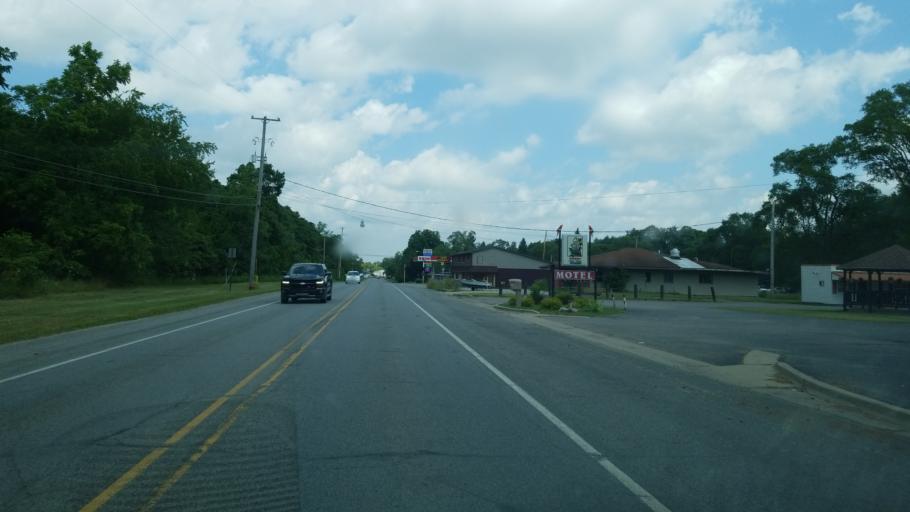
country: US
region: Michigan
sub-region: Montcalm County
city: Howard City
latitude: 43.3900
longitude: -85.4719
